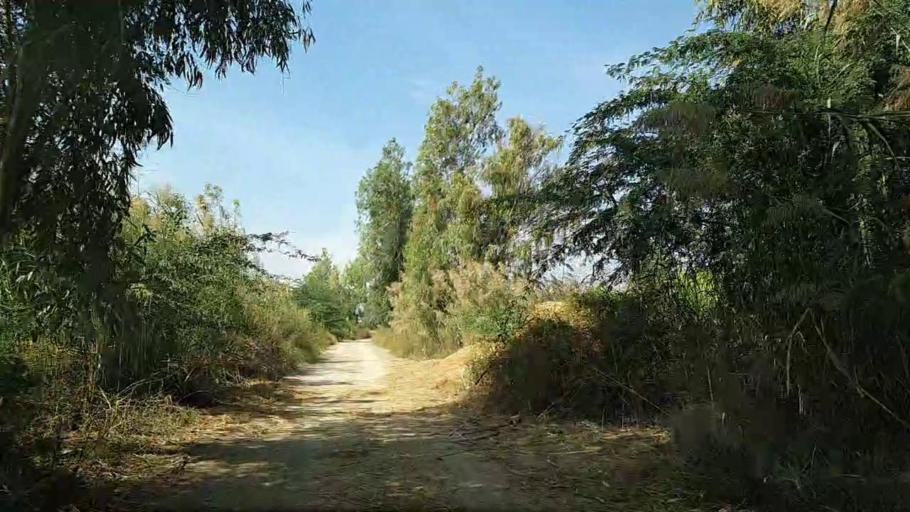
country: PK
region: Sindh
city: Daro Mehar
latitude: 24.7021
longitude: 68.1498
